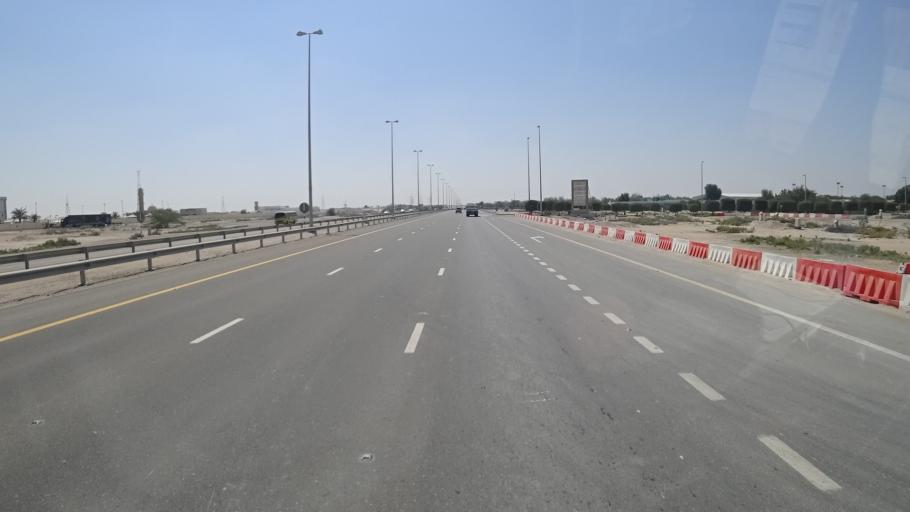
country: AE
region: Abu Dhabi
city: Abu Dhabi
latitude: 24.3103
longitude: 54.6744
